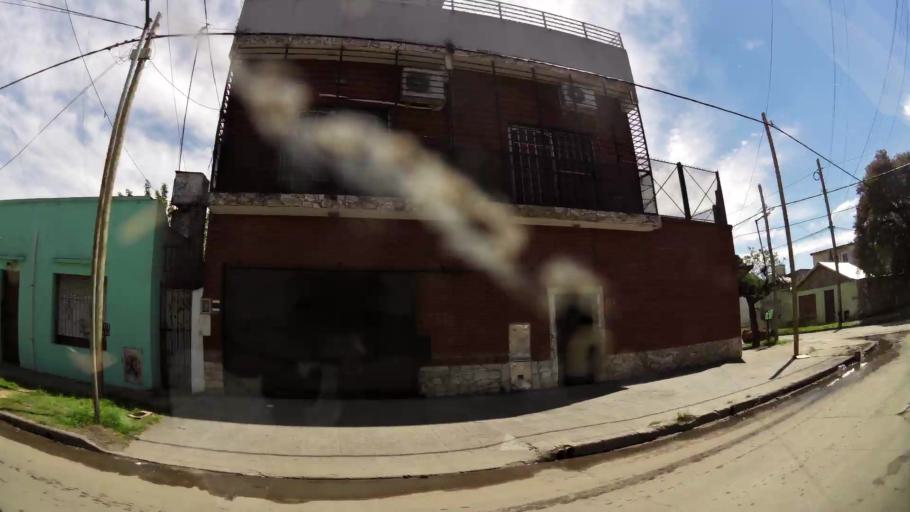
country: AR
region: Buenos Aires
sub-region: Partido de Quilmes
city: Quilmes
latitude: -34.7469
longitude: -58.2939
